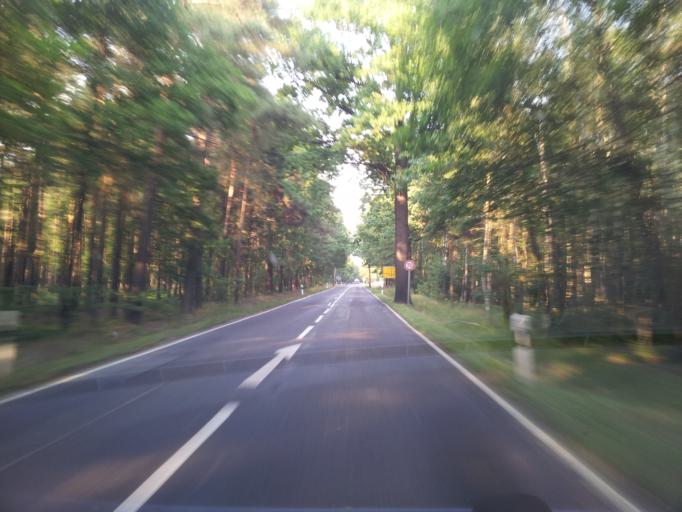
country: DE
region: Saxony
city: Schwepnitz
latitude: 51.3403
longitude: 13.9941
